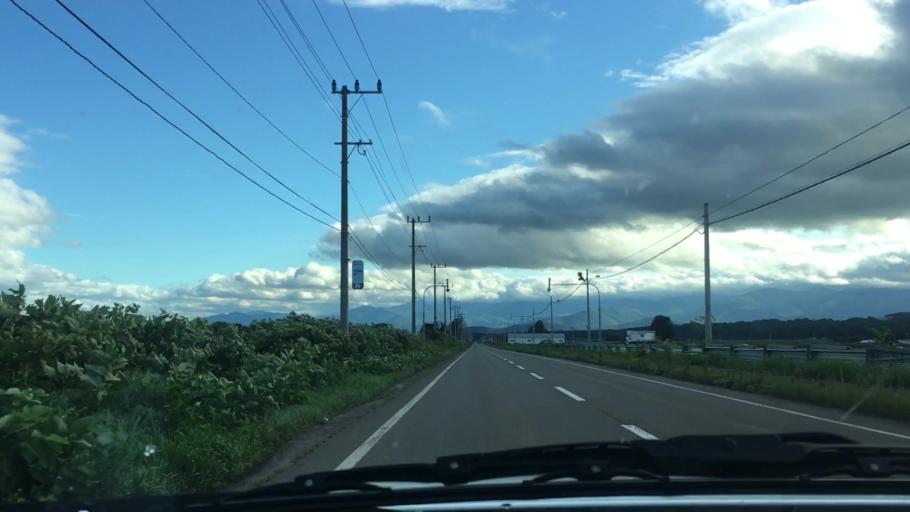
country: JP
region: Hokkaido
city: Otofuke
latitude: 43.1581
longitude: 142.9032
